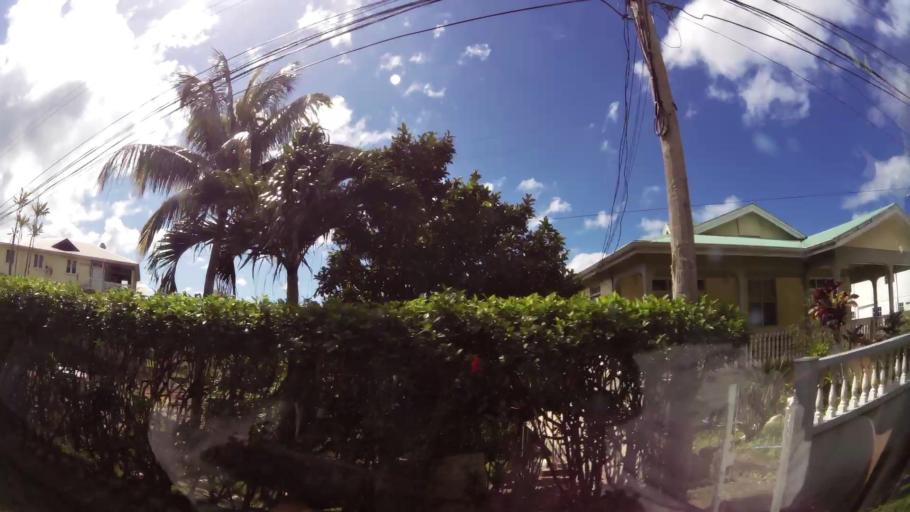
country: DM
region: Saint John
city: Portsmouth
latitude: 15.6069
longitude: -61.4637
